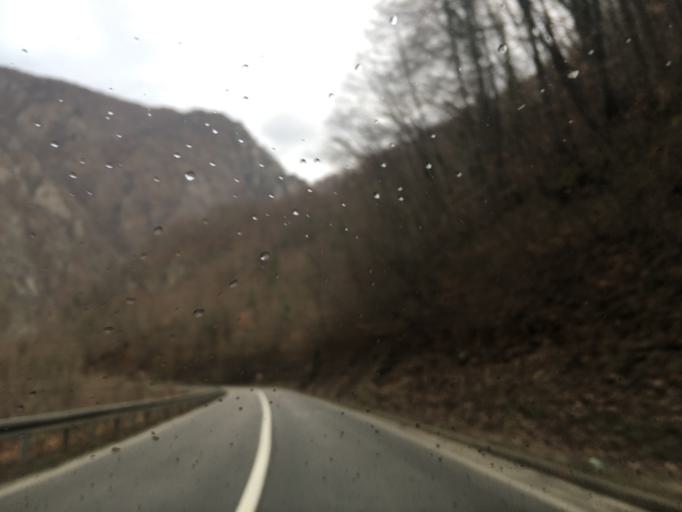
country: RS
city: Sokolovo Brdo
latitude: 43.1958
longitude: 19.7650
